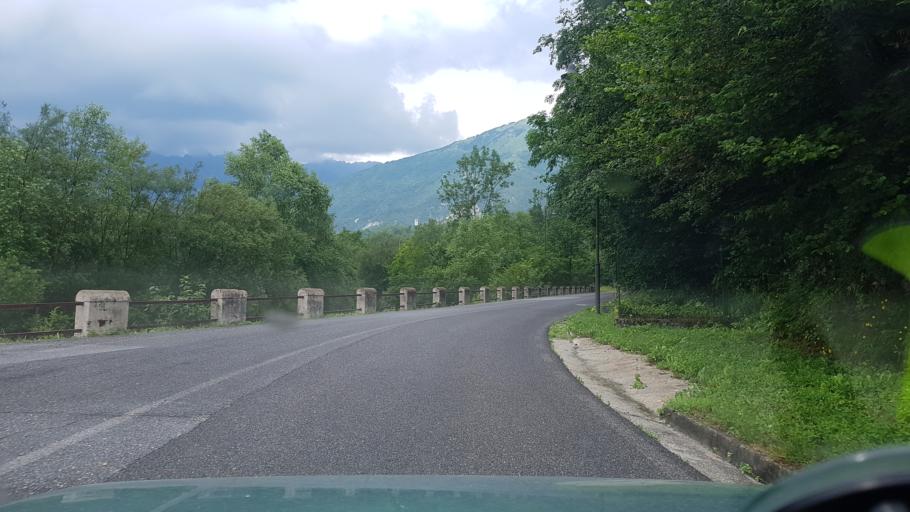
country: IT
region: Friuli Venezia Giulia
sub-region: Provincia di Udine
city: Lusevera
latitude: 46.2611
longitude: 13.2573
